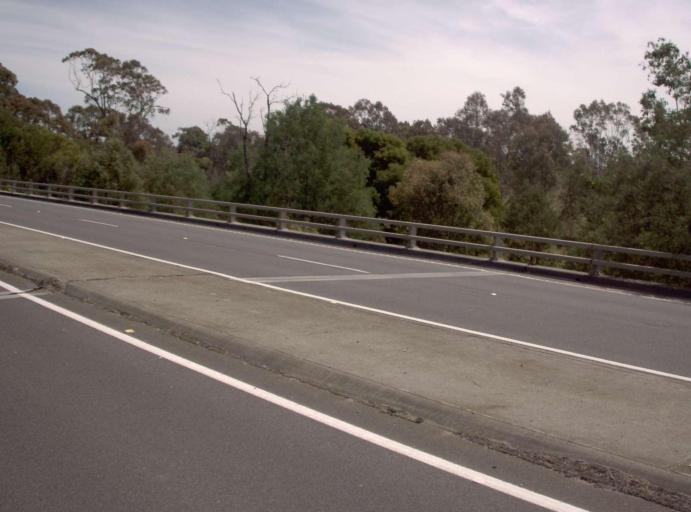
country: AU
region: Victoria
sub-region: Wellington
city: Heyfield
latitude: -38.1474
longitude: 146.7908
